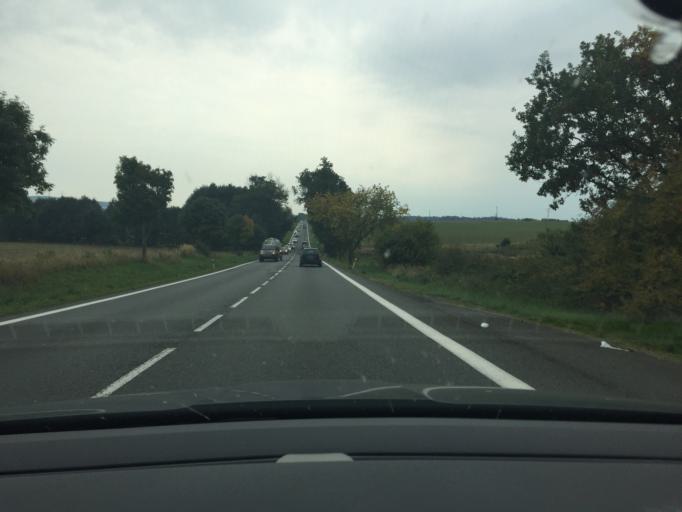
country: CZ
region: Central Bohemia
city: Milin
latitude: 49.6184
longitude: 14.0539
